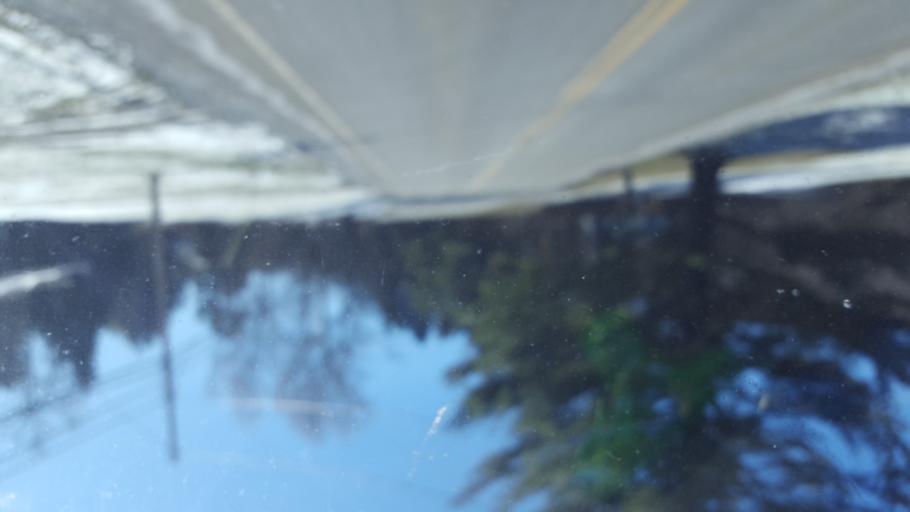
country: US
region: New York
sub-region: Allegany County
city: Wellsville
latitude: 42.0848
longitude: -77.9113
